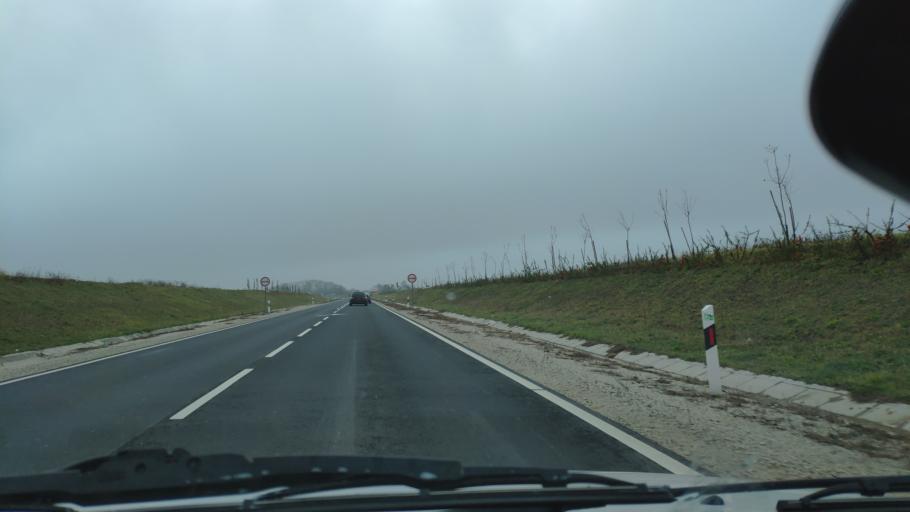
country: HU
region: Zala
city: Nagykanizsa
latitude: 46.4555
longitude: 17.0329
